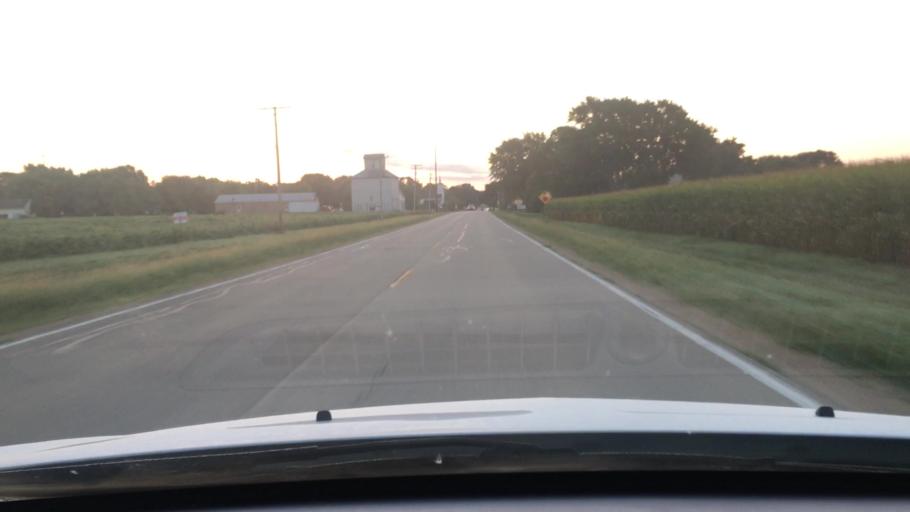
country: US
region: Illinois
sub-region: Ogle County
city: Rochelle
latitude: 41.8475
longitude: -89.0282
